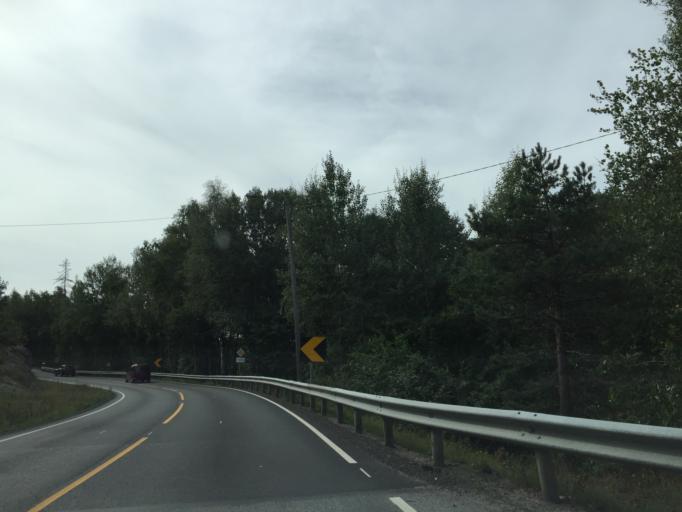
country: NO
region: Ostfold
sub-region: Fredrikstad
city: Fredrikstad
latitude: 59.1049
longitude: 10.9040
